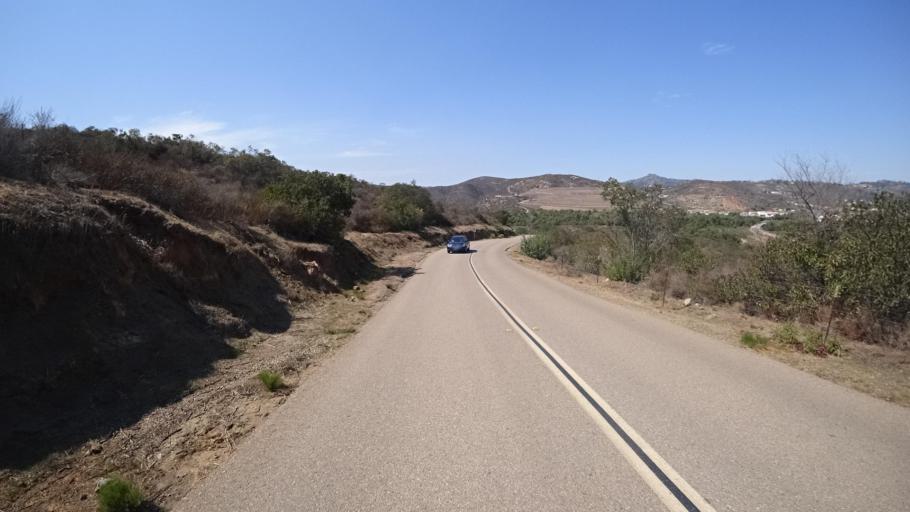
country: US
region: California
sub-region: San Diego County
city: Rancho San Diego
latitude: 32.7273
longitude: -116.9364
